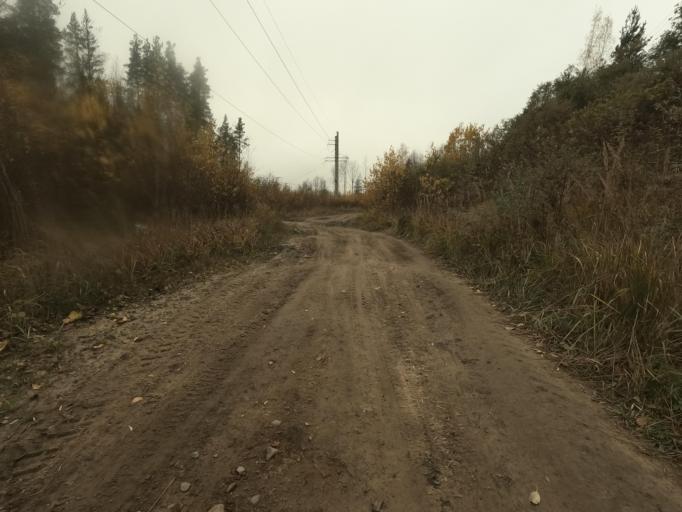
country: RU
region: Leningrad
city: Pavlovo
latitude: 59.7705
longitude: 30.9075
